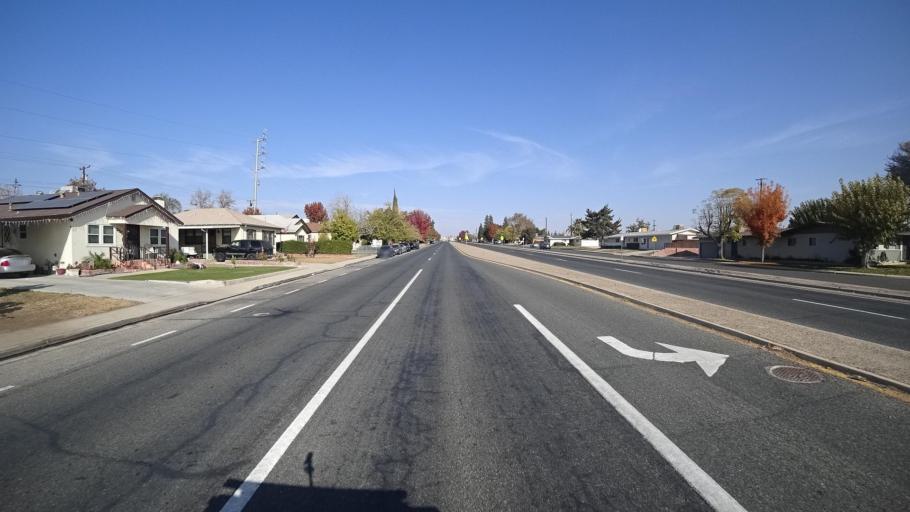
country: US
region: California
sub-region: Kern County
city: Oildale
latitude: 35.4297
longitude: -119.0123
